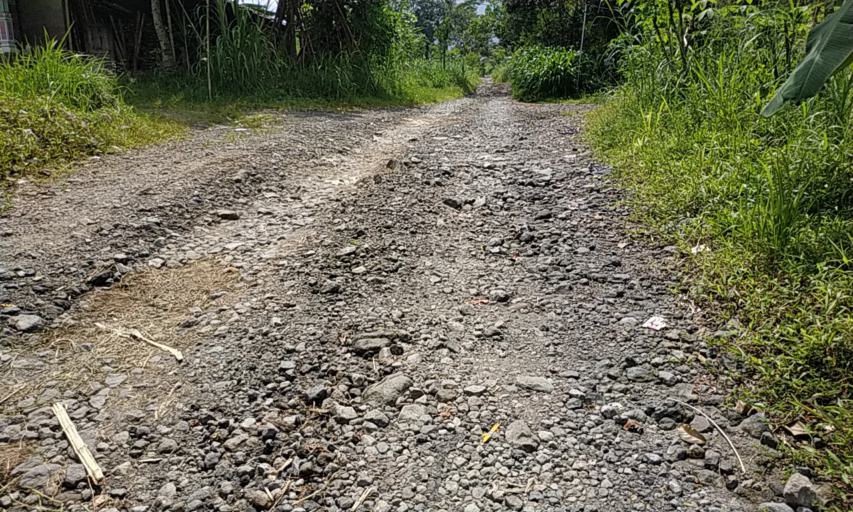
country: ID
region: Central Java
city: Jogonalan
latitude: -7.6317
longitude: 110.4862
